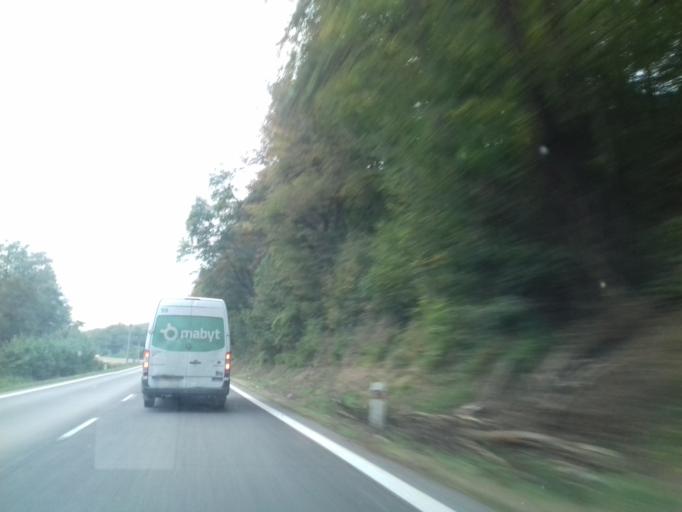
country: SK
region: Trenciansky
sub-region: Okres Trencin
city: Trencin
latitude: 48.9389
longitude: 17.9372
